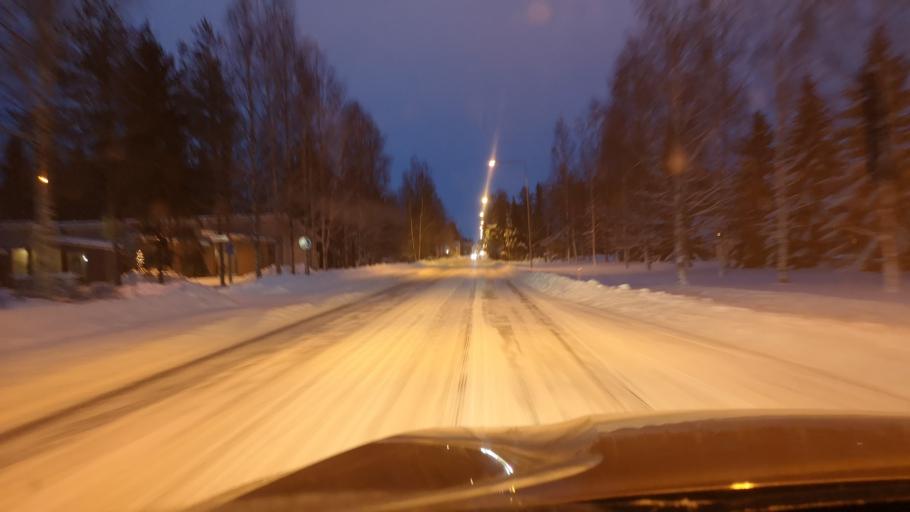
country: FI
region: Varsinais-Suomi
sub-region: Loimaa
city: Loimaa
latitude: 60.8565
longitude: 23.0652
